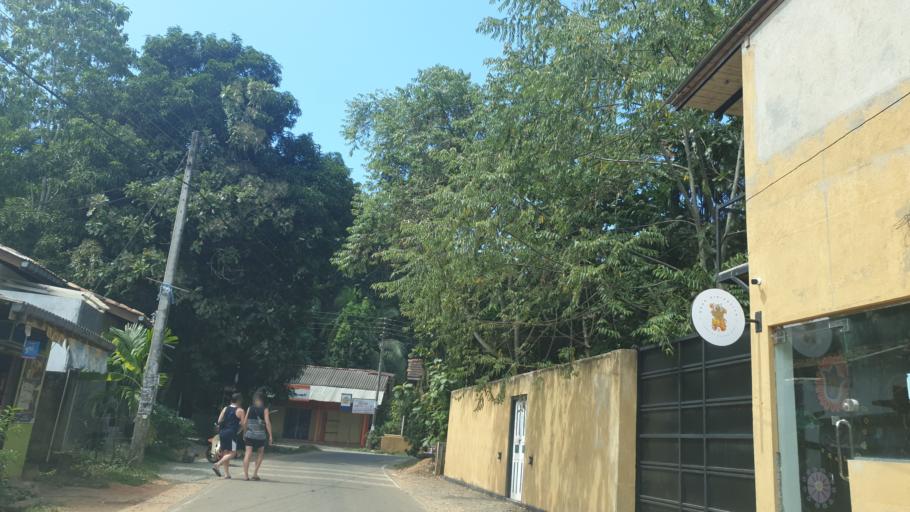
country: LK
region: Southern
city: Tangalla
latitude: 5.9663
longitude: 80.7077
